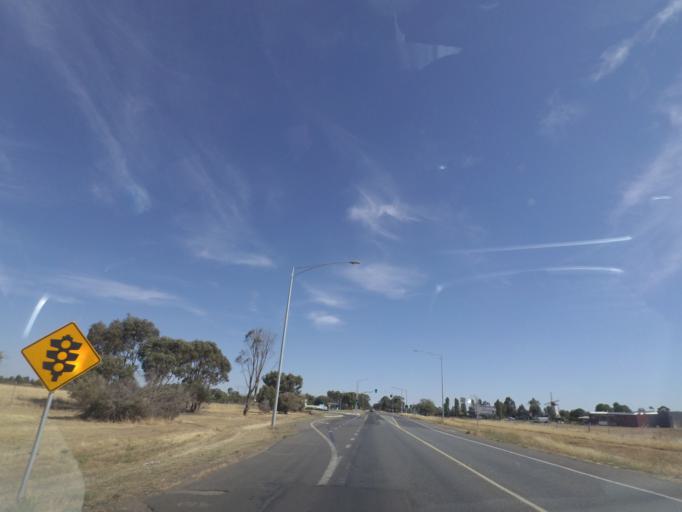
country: AU
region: Victoria
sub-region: Greater Shepparton
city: Shepparton
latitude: -36.4340
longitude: 145.3888
